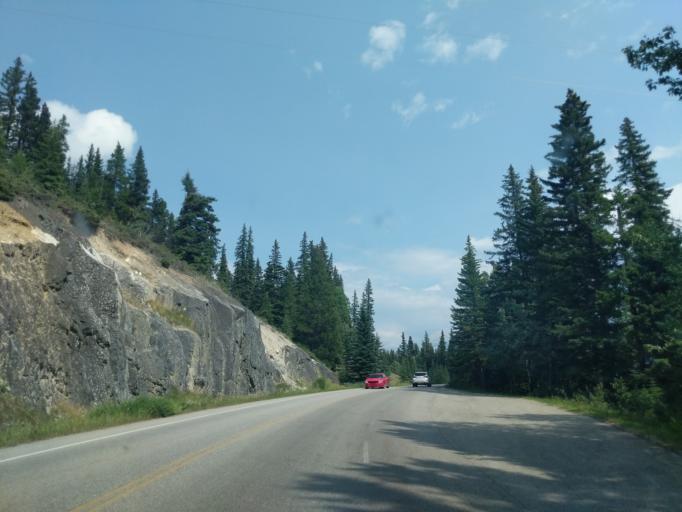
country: CA
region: Alberta
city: Banff
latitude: 51.1686
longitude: -115.6868
